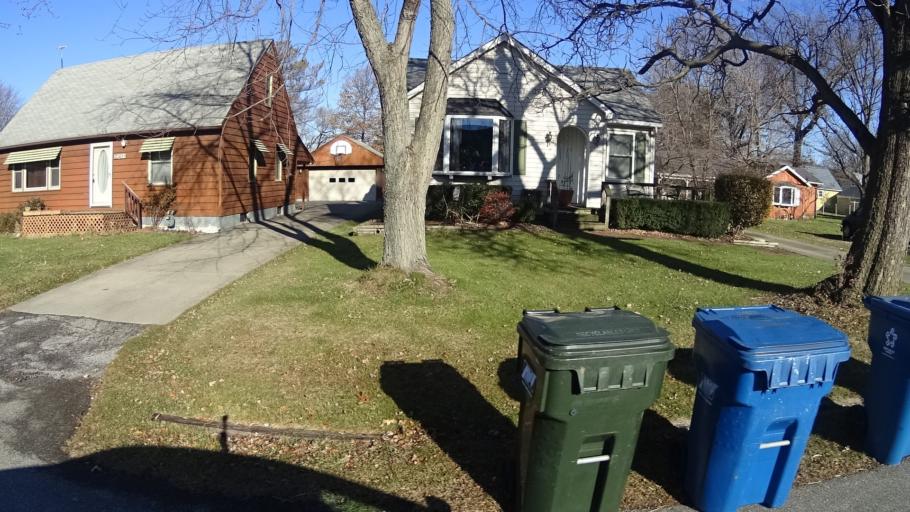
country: US
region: Ohio
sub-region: Lorain County
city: Sheffield
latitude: 41.4507
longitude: -82.1006
